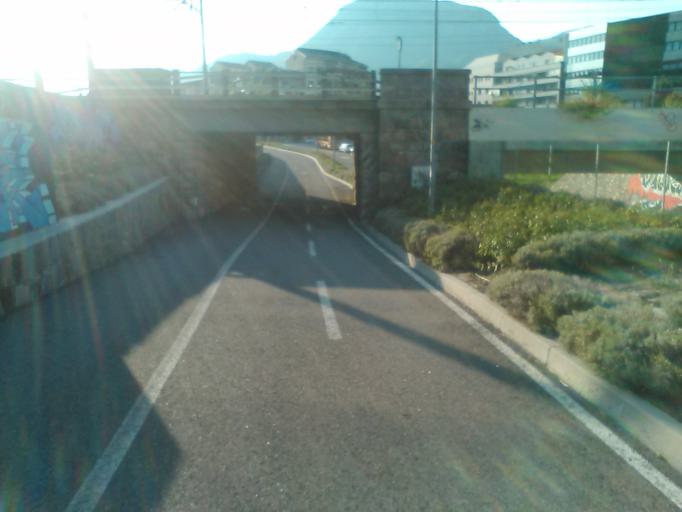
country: IT
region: Trentino-Alto Adige
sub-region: Bolzano
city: Bolzano
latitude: 46.4941
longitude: 11.3554
